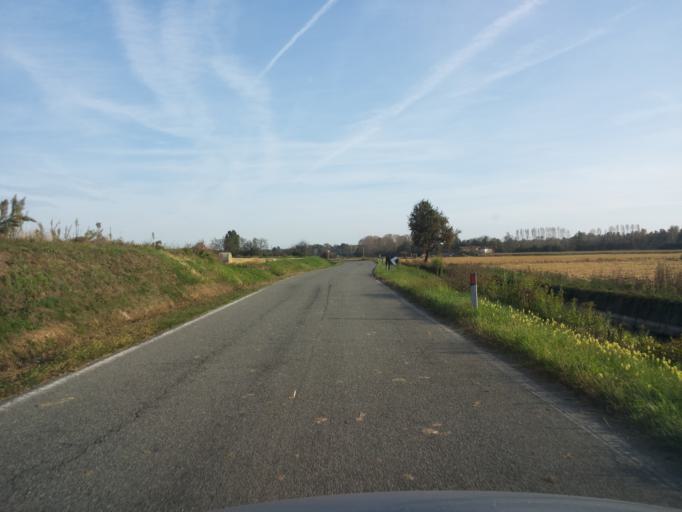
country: IT
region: Piedmont
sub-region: Provincia di Biella
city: Salussola
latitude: 45.4408
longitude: 8.1595
